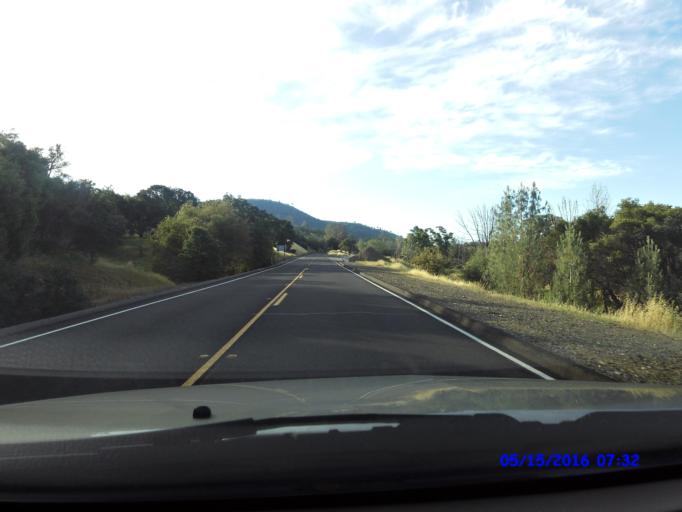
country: US
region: California
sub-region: Tuolumne County
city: Tuolumne City
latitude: 37.6999
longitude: -120.1873
